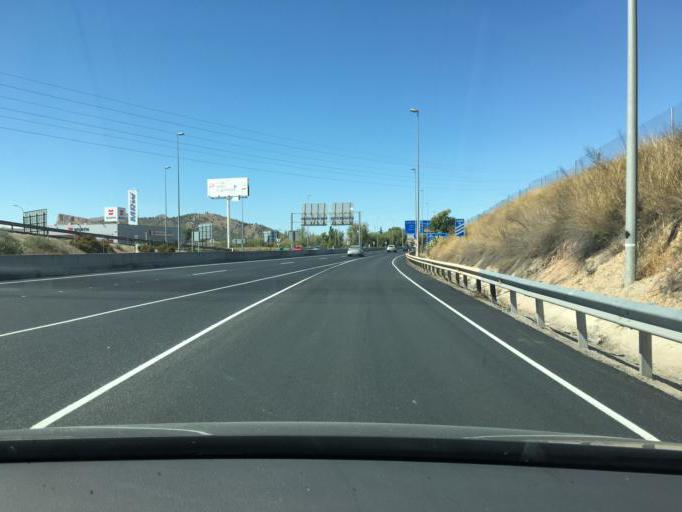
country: ES
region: Andalusia
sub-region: Provincia de Granada
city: Albolote
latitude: 37.2371
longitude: -3.6466
